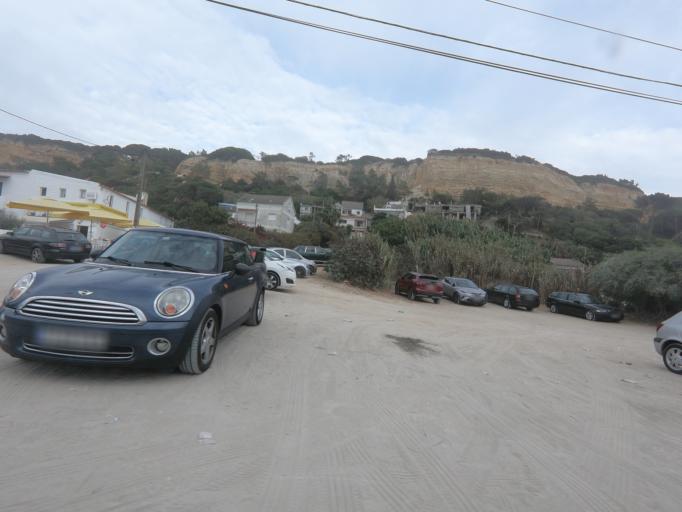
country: PT
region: Setubal
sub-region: Almada
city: Charneca
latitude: 38.5714
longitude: -9.1949
